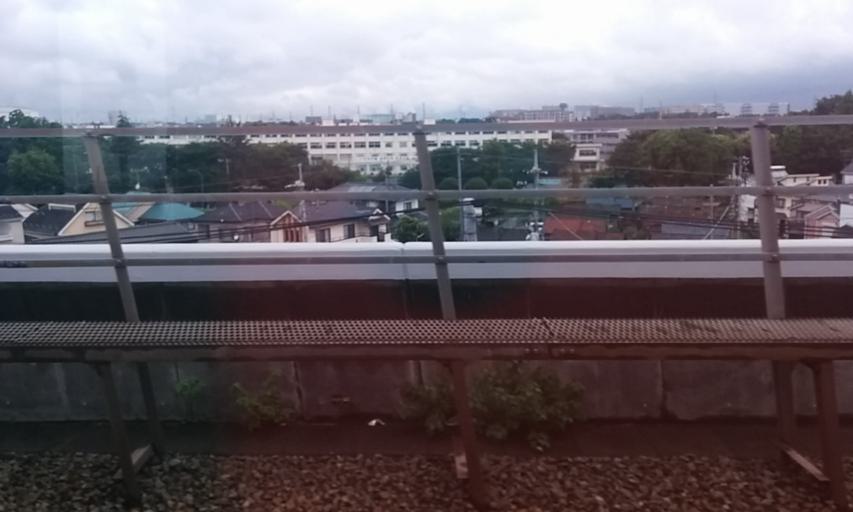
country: JP
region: Tokyo
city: Hachioji
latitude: 35.6431
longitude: 139.3574
